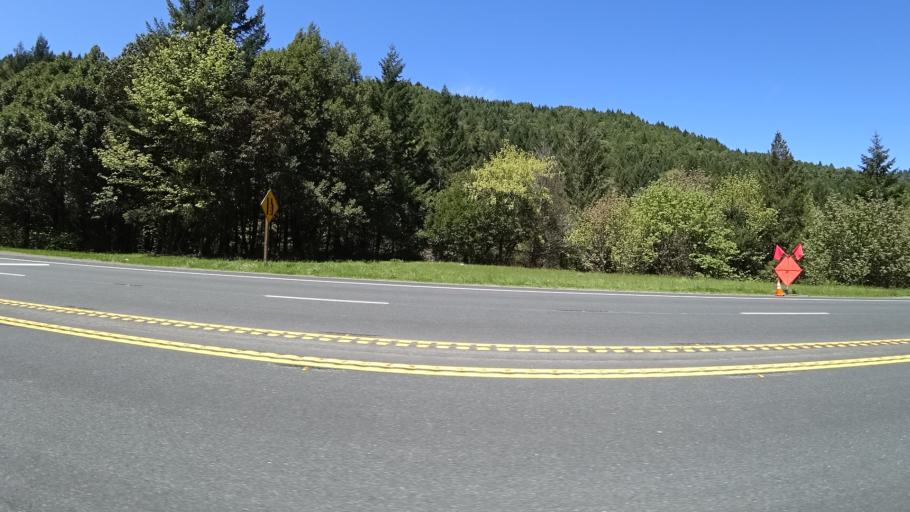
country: US
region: California
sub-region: Humboldt County
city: Willow Creek
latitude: 40.9119
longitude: -123.7055
